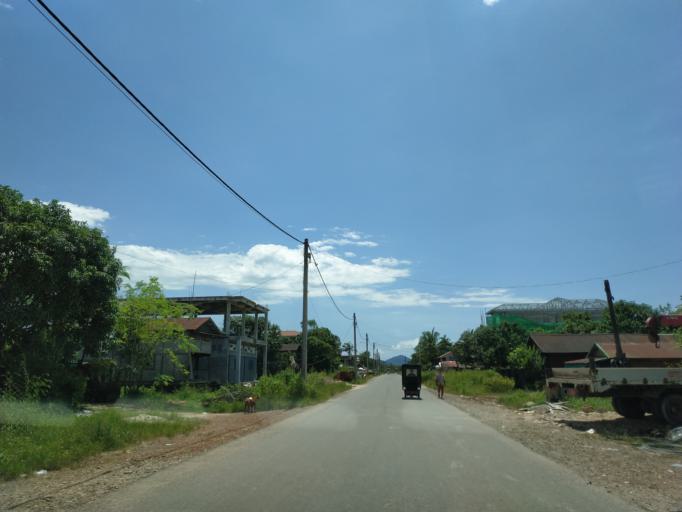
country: MM
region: Tanintharyi
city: Dawei
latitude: 14.0949
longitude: 98.1871
